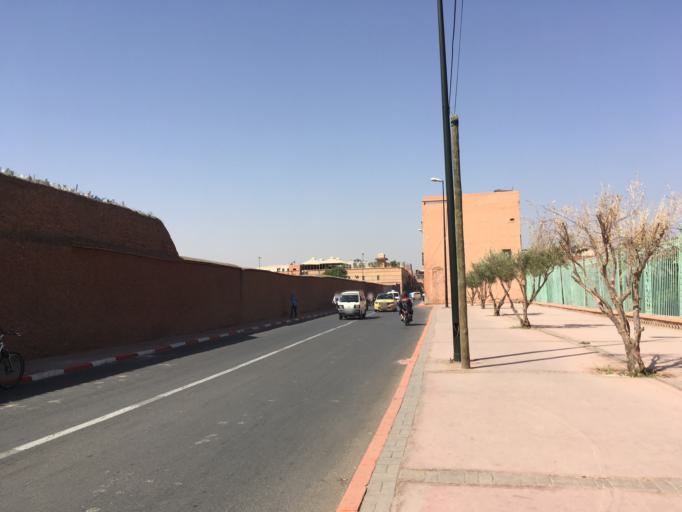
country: MA
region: Marrakech-Tensift-Al Haouz
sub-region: Marrakech
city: Marrakesh
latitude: 31.6218
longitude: -7.9792
